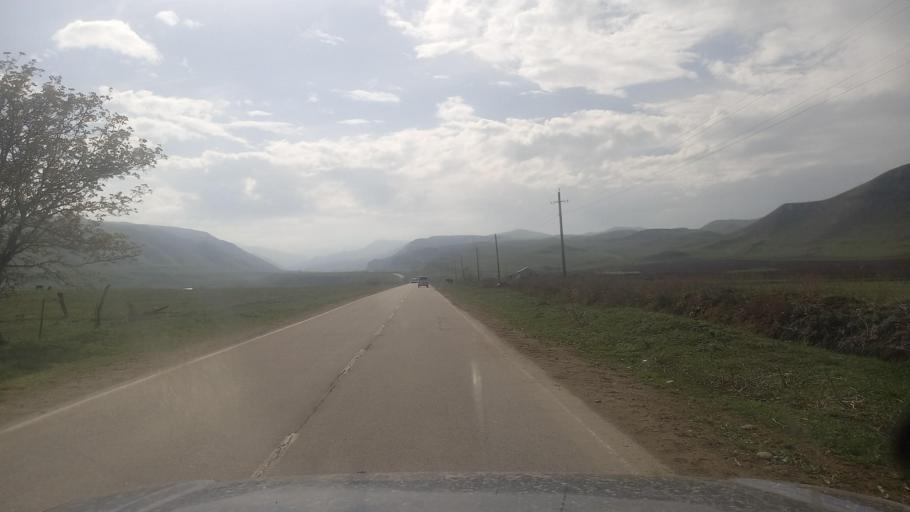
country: RU
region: Kabardino-Balkariya
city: Kamennomostskoye
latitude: 43.7359
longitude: 43.0077
